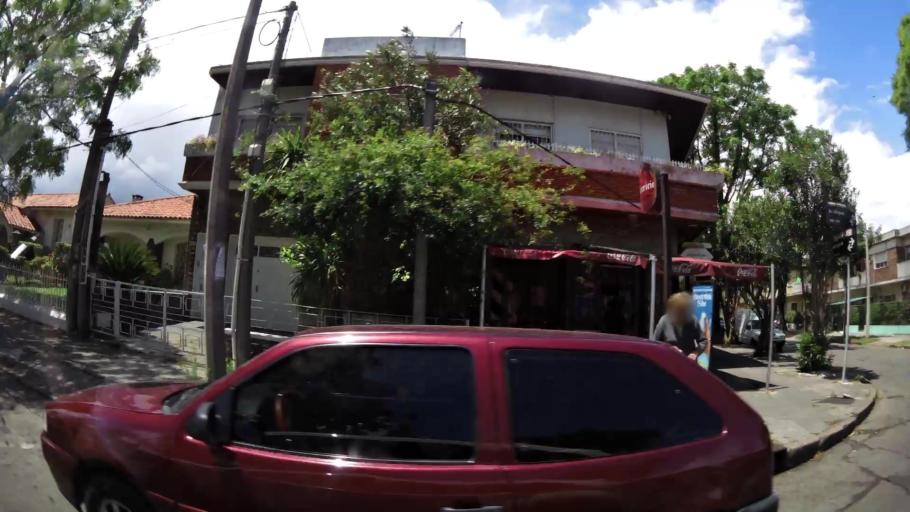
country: UY
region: Montevideo
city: Montevideo
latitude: -34.8642
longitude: -56.1867
